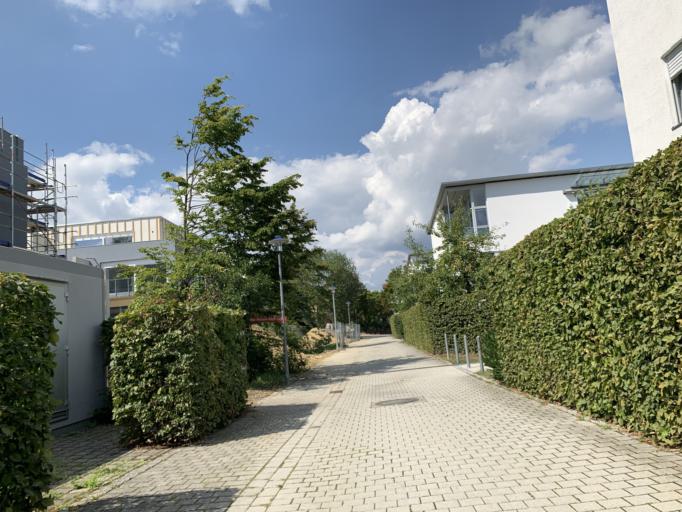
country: DE
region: Bavaria
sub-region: Upper Bavaria
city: Freising
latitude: 48.4075
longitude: 11.7390
